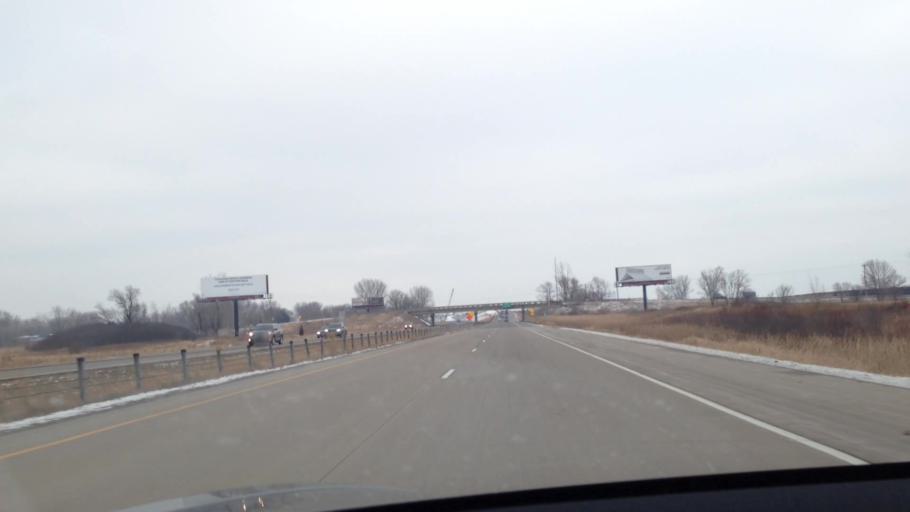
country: US
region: Minnesota
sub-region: Anoka County
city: Centerville
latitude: 45.2124
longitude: -93.0374
